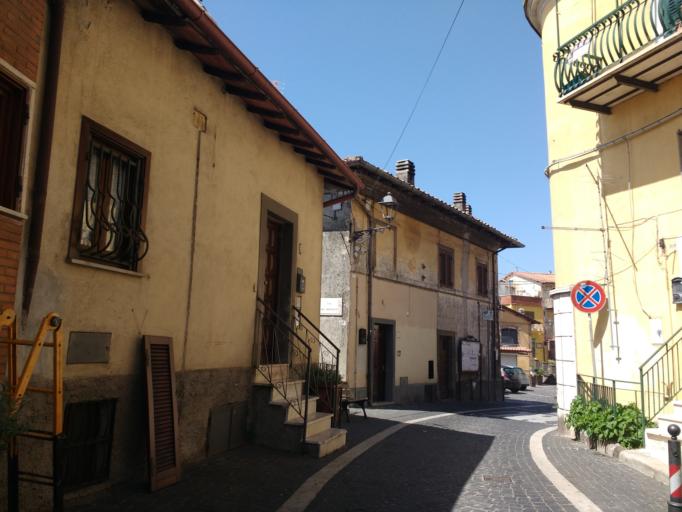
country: IT
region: Latium
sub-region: Citta metropolitana di Roma Capitale
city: Rocca di Papa
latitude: 41.7606
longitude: 12.7088
